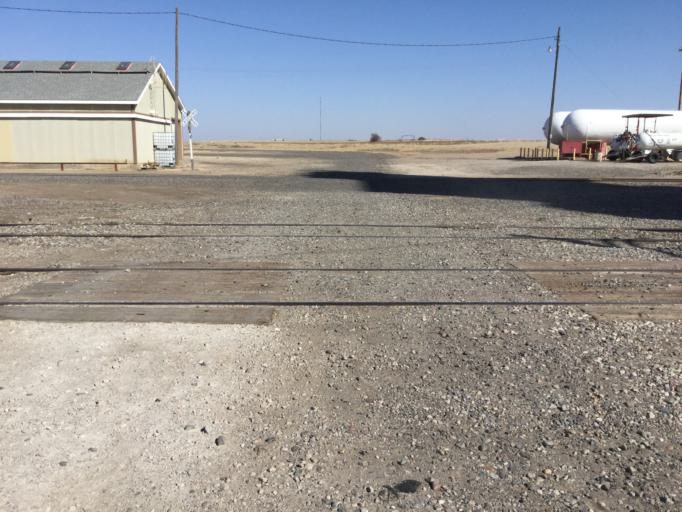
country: US
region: Kansas
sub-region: Rush County
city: La Crosse
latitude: 38.4669
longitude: -99.3187
